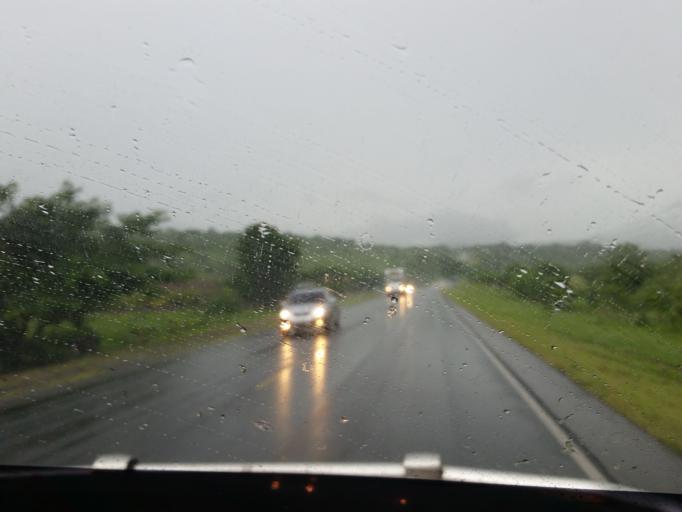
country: NI
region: Matagalpa
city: Ciudad Dario
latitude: 12.7642
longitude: -86.1247
